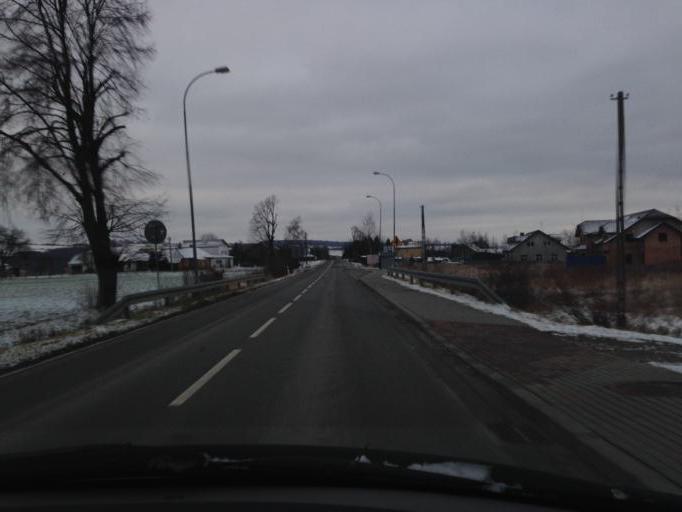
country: PL
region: Lesser Poland Voivodeship
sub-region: Powiat gorlicki
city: Moszczenica
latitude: 49.7041
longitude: 21.1194
